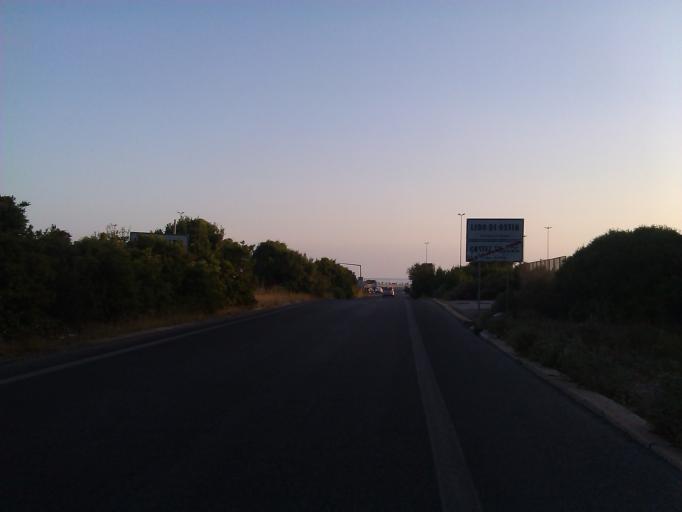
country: IT
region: Latium
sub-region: Citta metropolitana di Roma Capitale
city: Lido di Ostia
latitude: 41.7162
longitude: 12.3191
